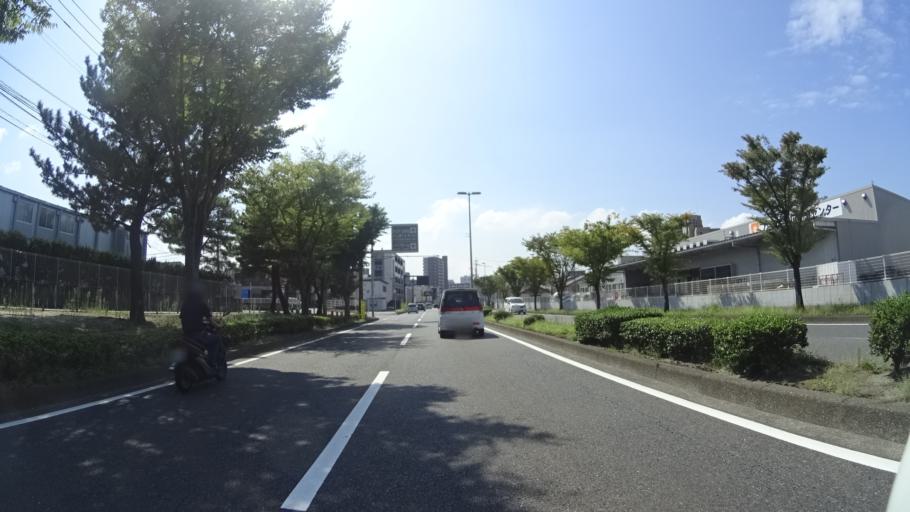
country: JP
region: Fukuoka
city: Kitakyushu
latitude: 33.8870
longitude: 130.8936
